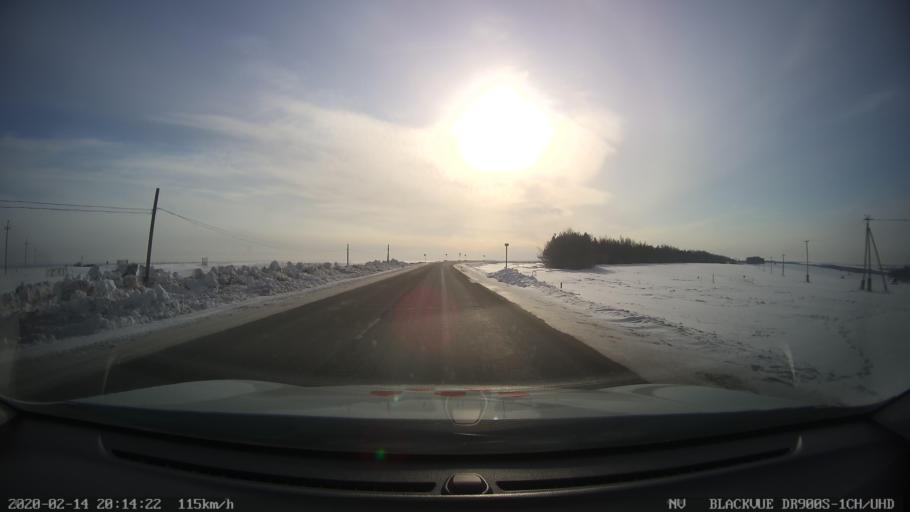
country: RU
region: Tatarstan
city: Verkhniy Uslon
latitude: 55.6457
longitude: 48.8748
